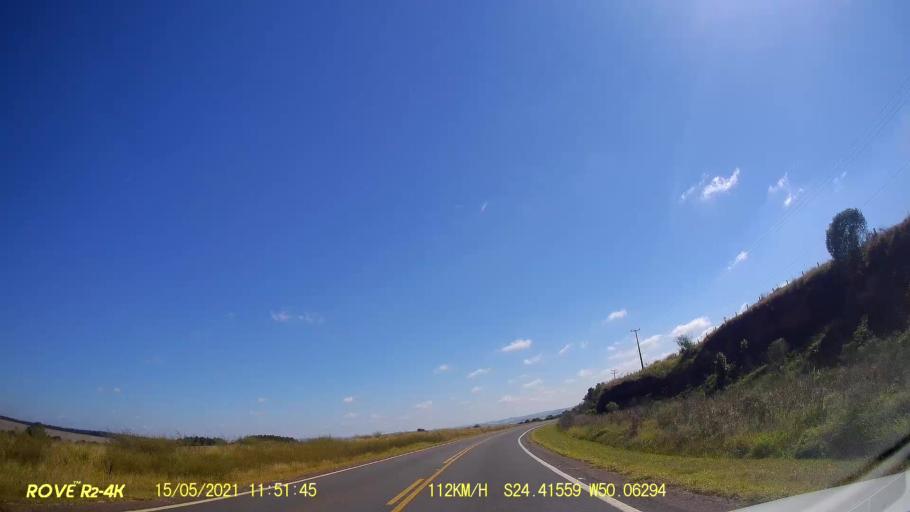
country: BR
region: Parana
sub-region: Pirai Do Sul
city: Pirai do Sul
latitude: -24.4099
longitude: -50.0672
